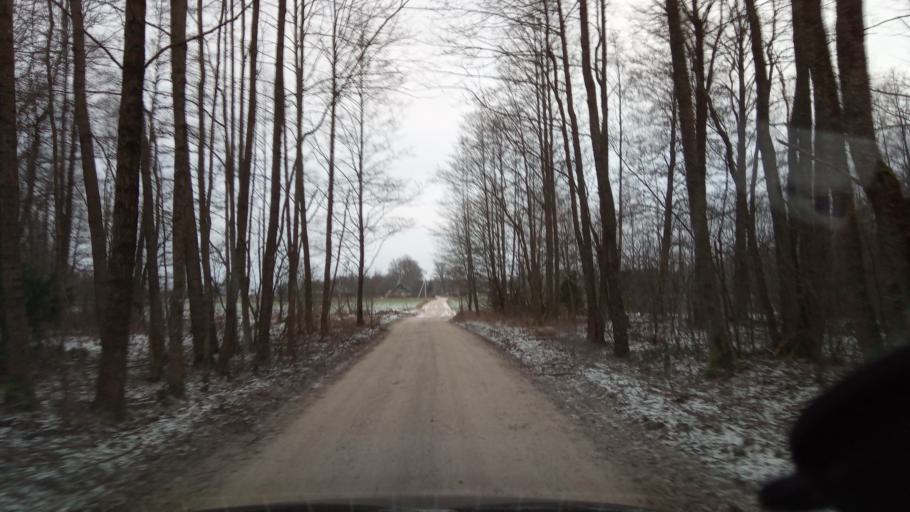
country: LT
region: Alytaus apskritis
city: Varena
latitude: 54.1240
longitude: 24.7056
